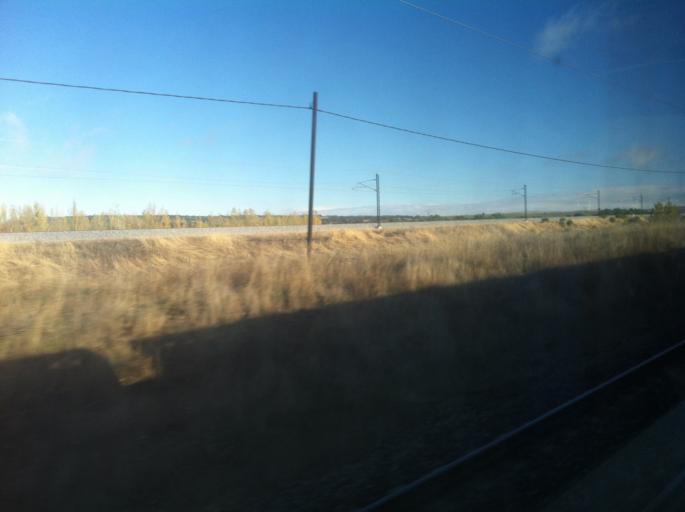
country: ES
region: Castille and Leon
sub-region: Provincia de Palencia
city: Villodrigo
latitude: 42.1590
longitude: -4.0855
